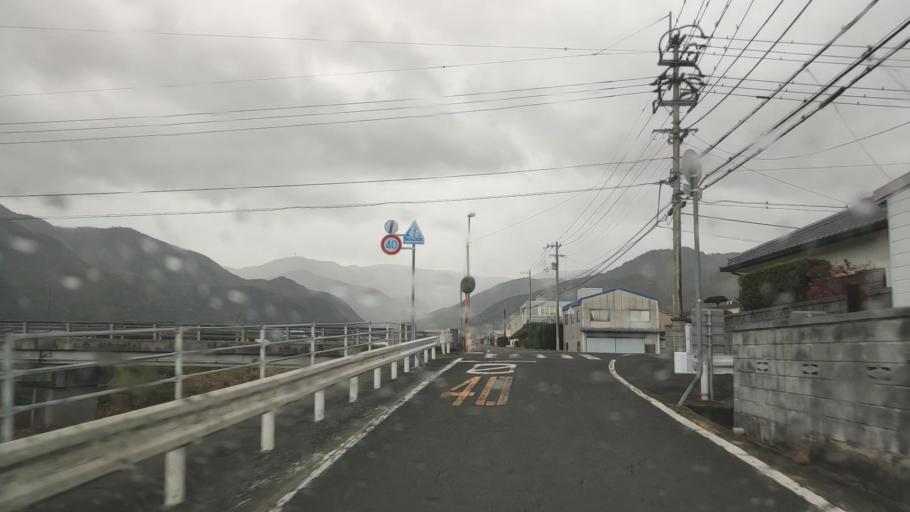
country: JP
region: Tokushima
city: Ishii
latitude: 34.2133
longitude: 134.4058
